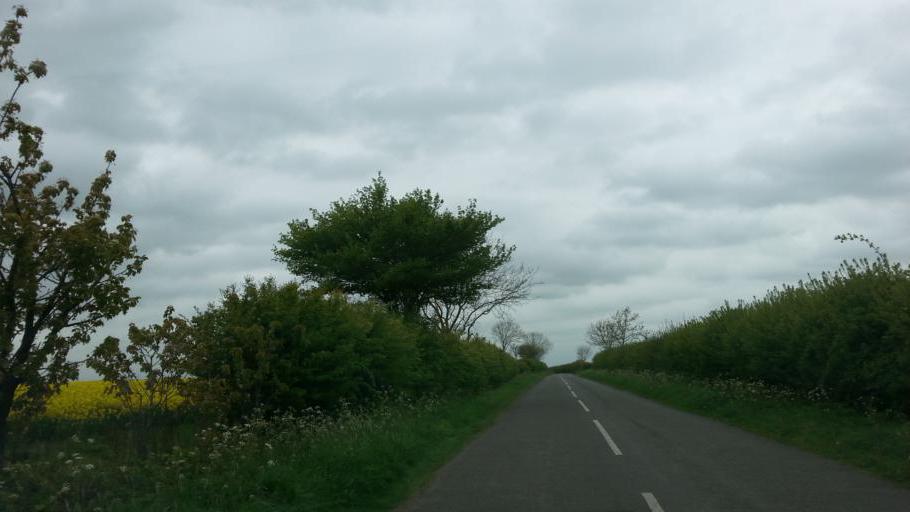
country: GB
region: England
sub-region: Lincolnshire
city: Grantham
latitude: 52.8675
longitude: -0.5389
